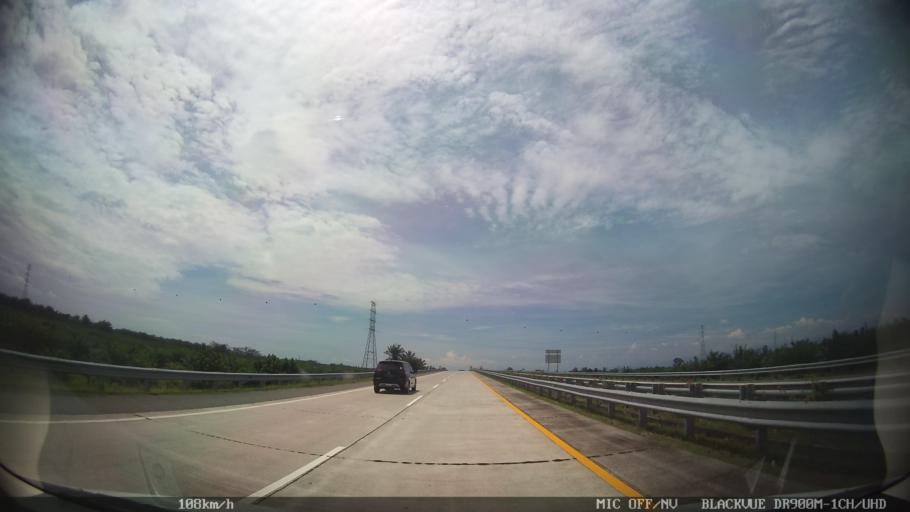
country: ID
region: North Sumatra
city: Percut
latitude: 3.5819
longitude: 98.8459
